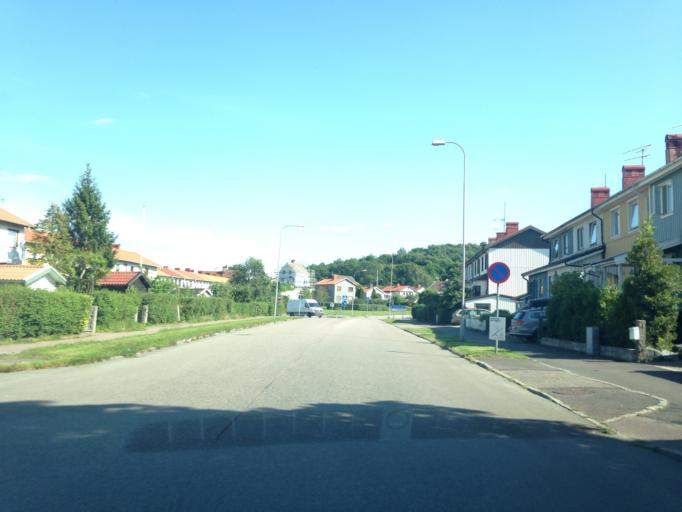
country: SE
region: Vaestra Goetaland
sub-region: Goteborg
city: Majorna
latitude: 57.7304
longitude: 11.9162
